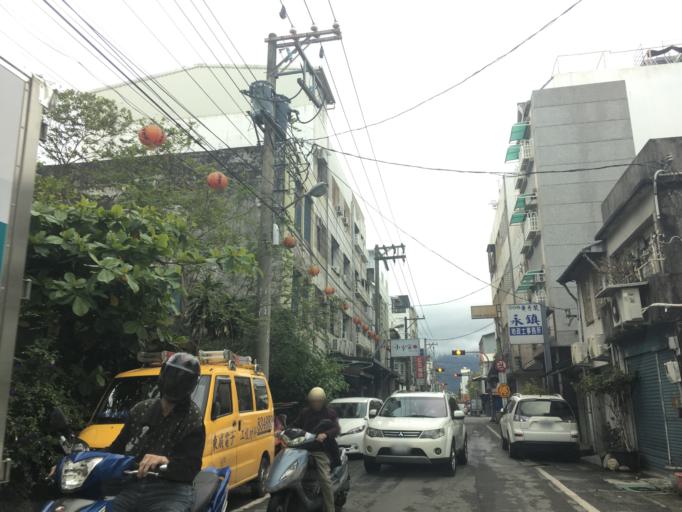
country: TW
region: Taiwan
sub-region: Hualien
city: Hualian
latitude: 23.9749
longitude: 121.6049
